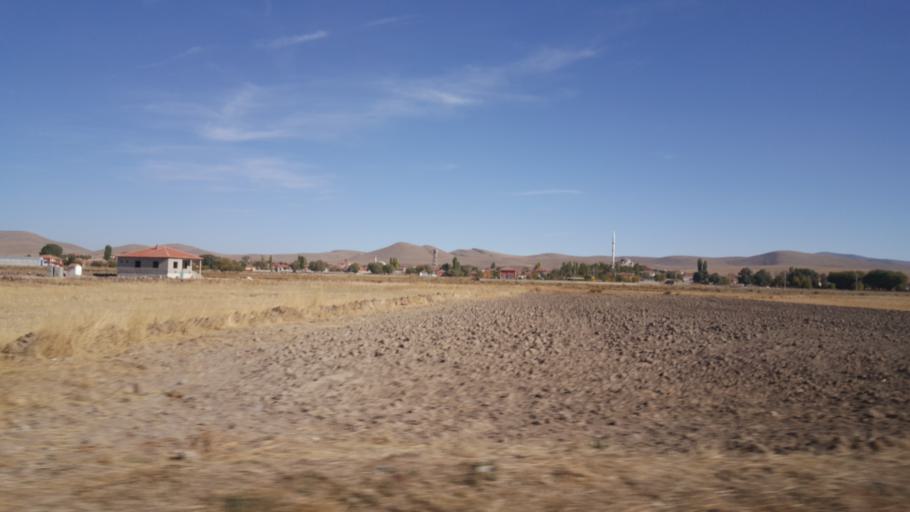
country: TR
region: Ankara
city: Altpinar
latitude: 39.2650
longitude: 32.7532
